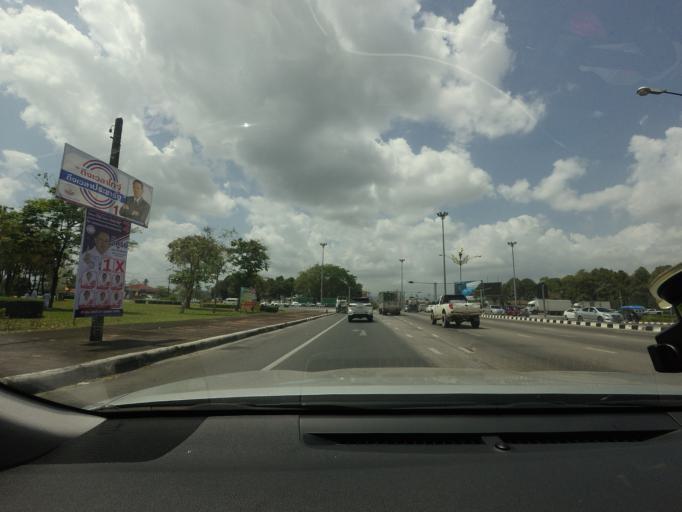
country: TH
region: Nakhon Si Thammarat
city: Nakhon Si Thammarat
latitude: 8.4339
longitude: 99.9225
